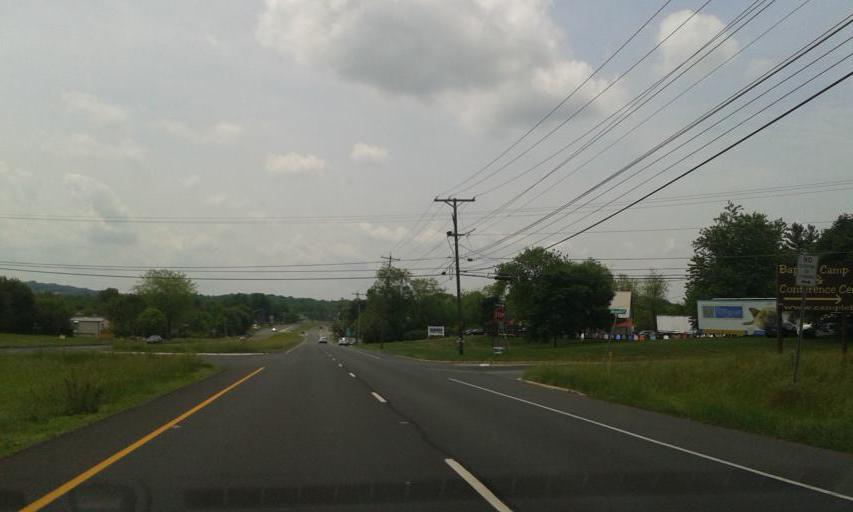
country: US
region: New Jersey
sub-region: Hunterdon County
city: Lebanon
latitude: 40.6448
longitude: -74.8199
